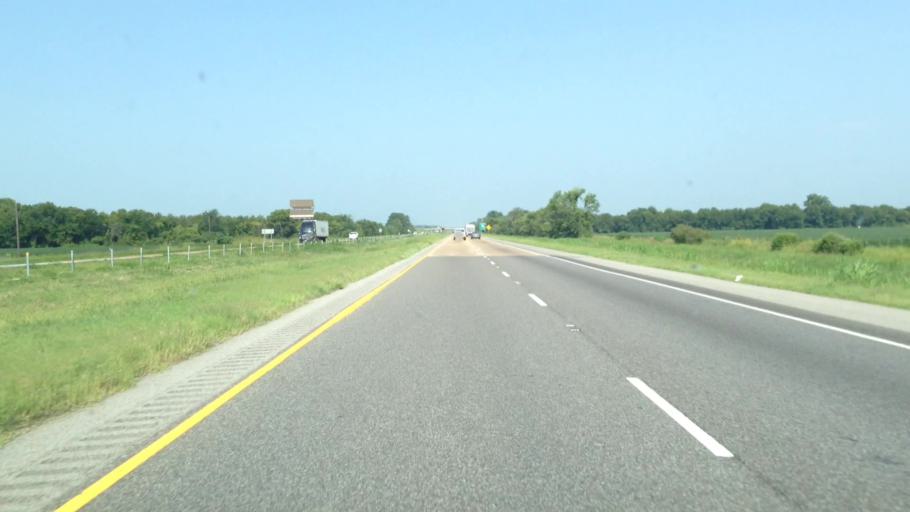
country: US
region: Mississippi
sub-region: Warren County
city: Vicksburg
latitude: 32.3271
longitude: -91.0064
